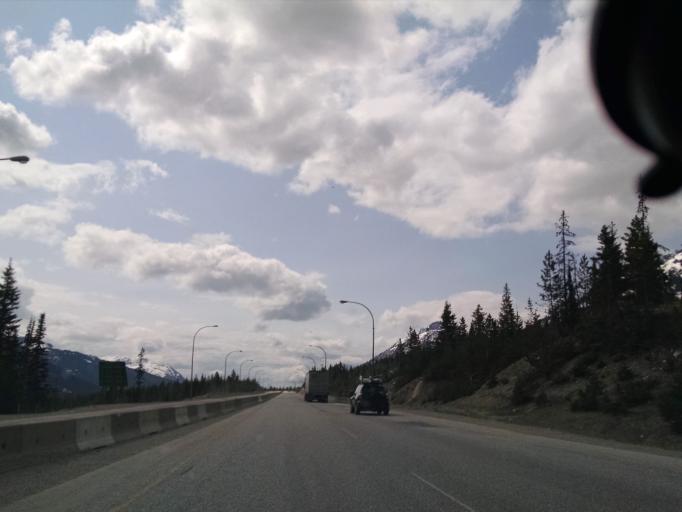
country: CA
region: British Columbia
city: Hope
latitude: 49.6193
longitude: -121.0425
